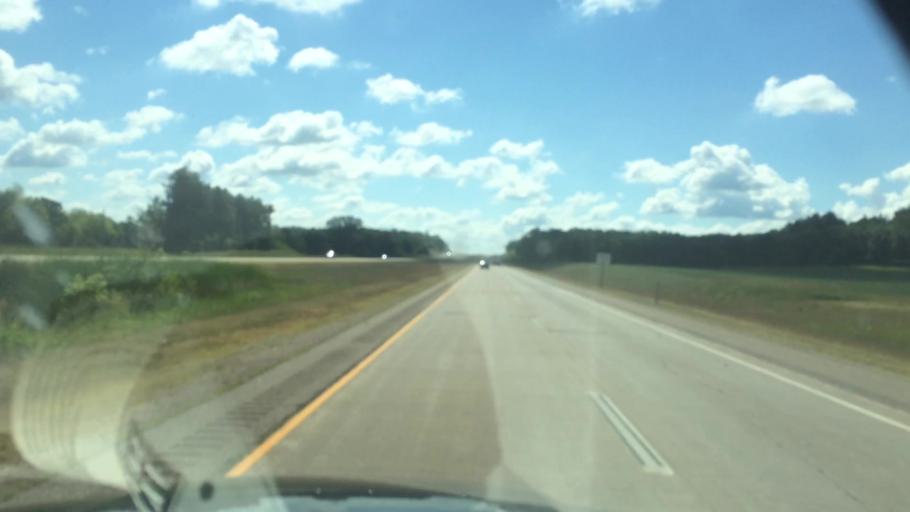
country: US
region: Wisconsin
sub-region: Waupaca County
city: King
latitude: 44.3936
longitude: -89.2015
